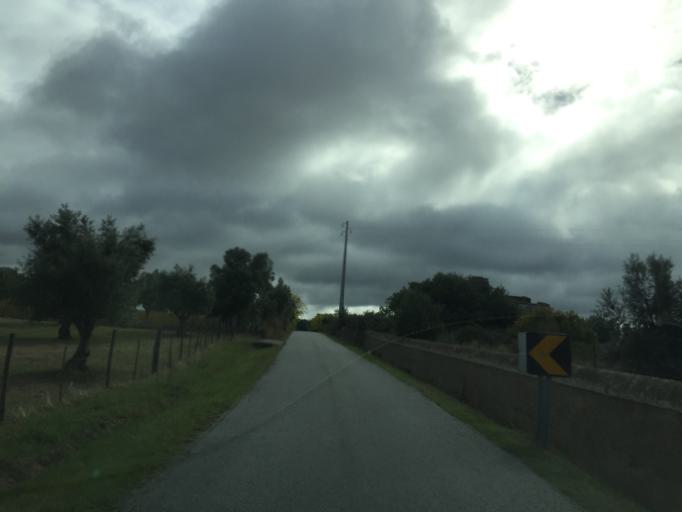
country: PT
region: Portalegre
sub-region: Alter do Chao
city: Alter do Chao
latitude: 39.2251
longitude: -7.6774
